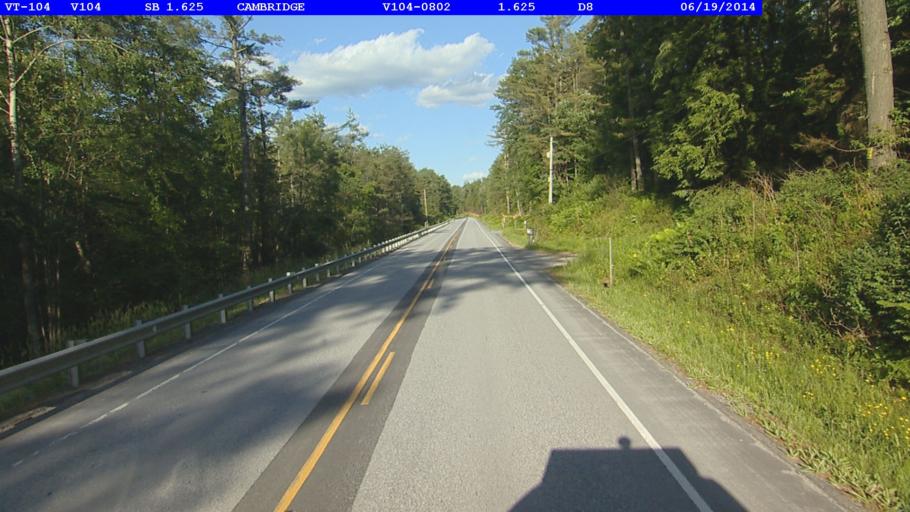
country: US
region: Vermont
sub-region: Chittenden County
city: Jericho
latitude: 44.6410
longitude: -72.9192
